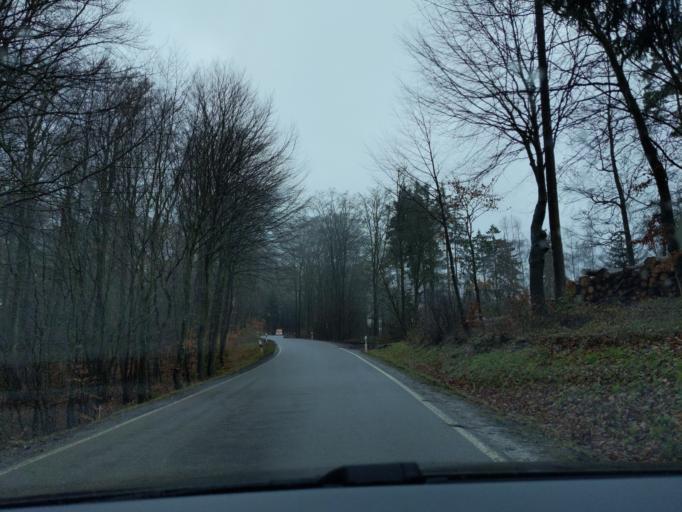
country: DE
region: Hesse
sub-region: Regierungsbezirk Kassel
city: Korbach
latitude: 51.2954
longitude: 8.9470
